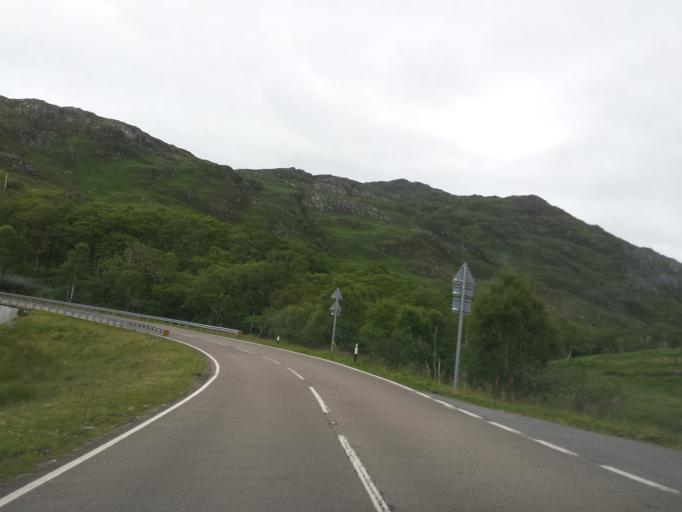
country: GB
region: Scotland
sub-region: Argyll and Bute
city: Isle Of Mull
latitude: 56.9004
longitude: -5.7530
